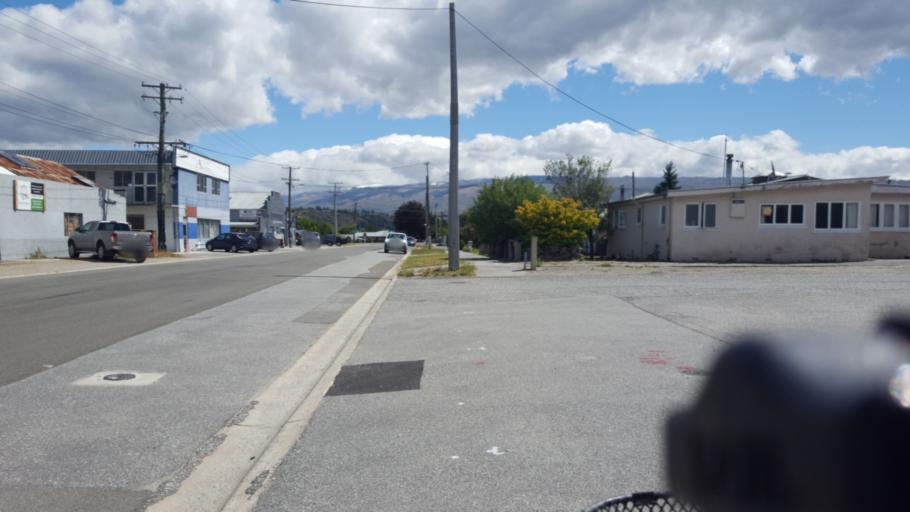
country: NZ
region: Otago
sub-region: Queenstown-Lakes District
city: Wanaka
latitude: -45.2466
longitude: 169.3935
